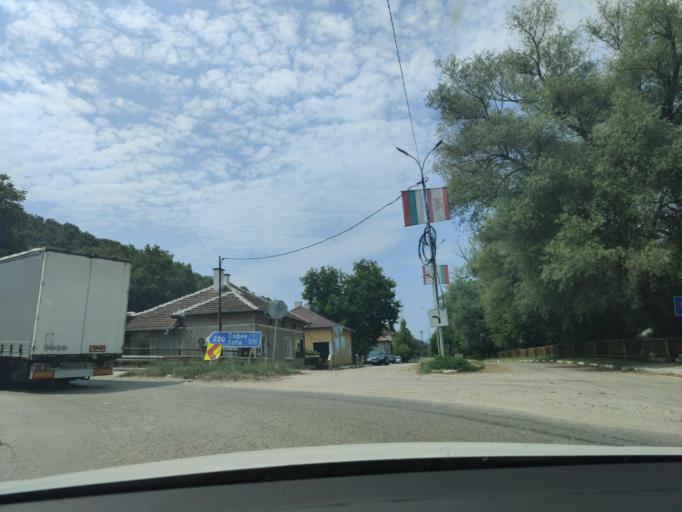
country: BG
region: Vidin
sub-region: Obshtina Dimovo
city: Dimovo
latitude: 43.7353
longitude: 22.7219
